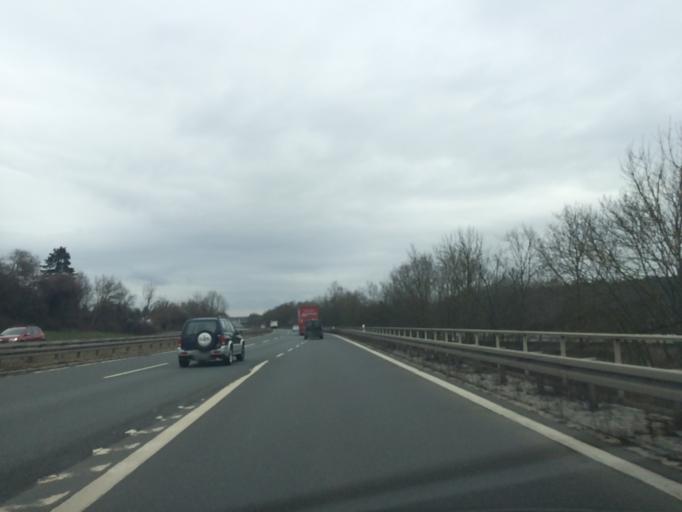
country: DE
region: Bavaria
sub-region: Regierungsbezirk Mittelfranken
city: Zirndorf
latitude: 49.4730
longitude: 10.9480
